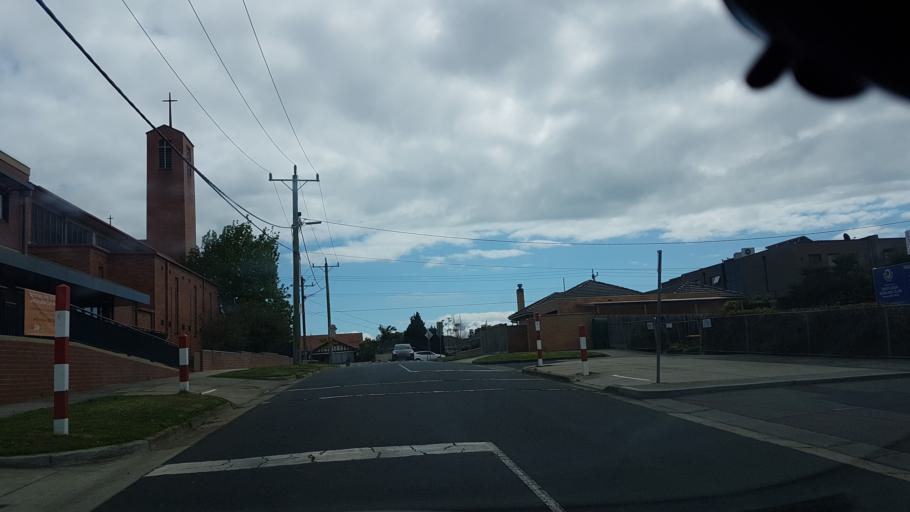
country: AU
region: Victoria
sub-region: Glen Eira
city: Bentleigh
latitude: -37.9224
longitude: 145.0420
